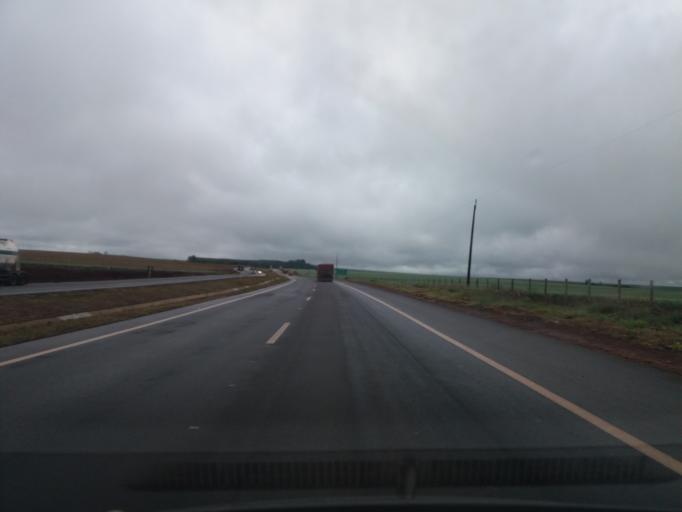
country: BR
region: Parana
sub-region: Cascavel
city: Cascavel
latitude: -25.0754
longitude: -53.5755
